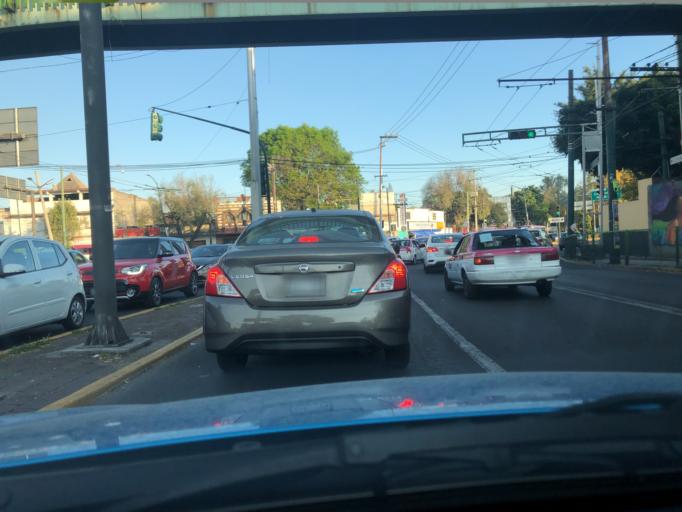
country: MX
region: Mexico City
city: Azcapotzalco
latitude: 19.4778
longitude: -99.1850
